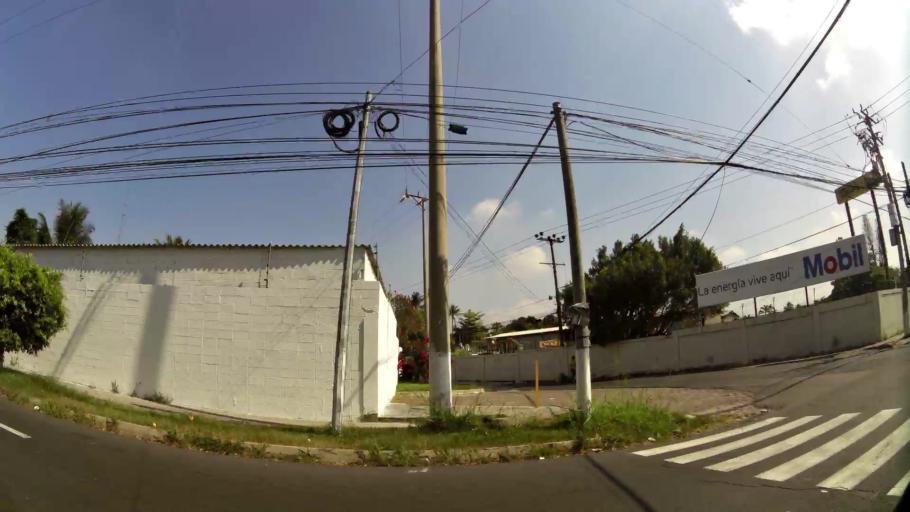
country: SV
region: La Libertad
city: Antiguo Cuscatlan
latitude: 13.6876
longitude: -89.2303
